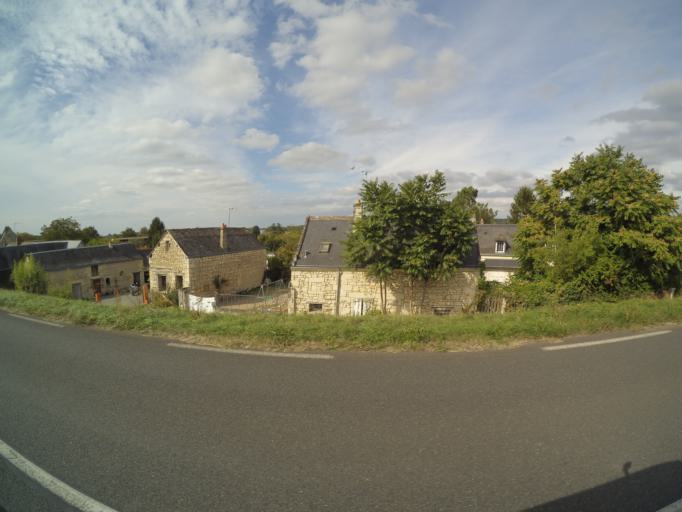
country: FR
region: Centre
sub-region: Departement d'Indre-et-Loire
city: Huismes
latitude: 47.2715
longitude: 0.3022
